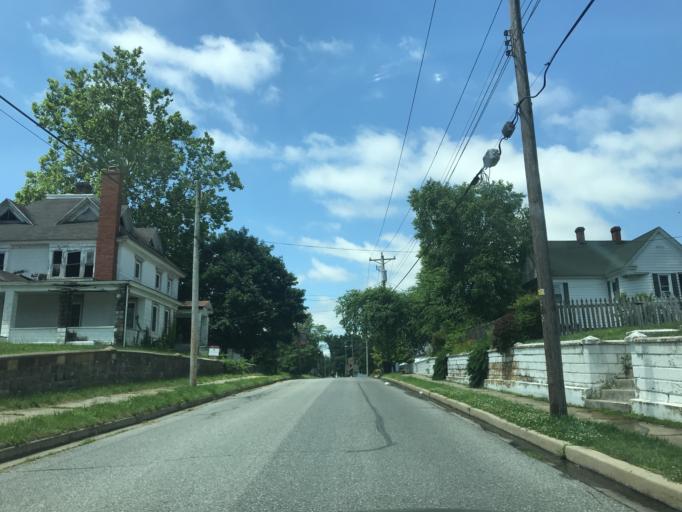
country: US
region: Maryland
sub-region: Caroline County
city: Federalsburg
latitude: 38.6914
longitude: -75.7772
